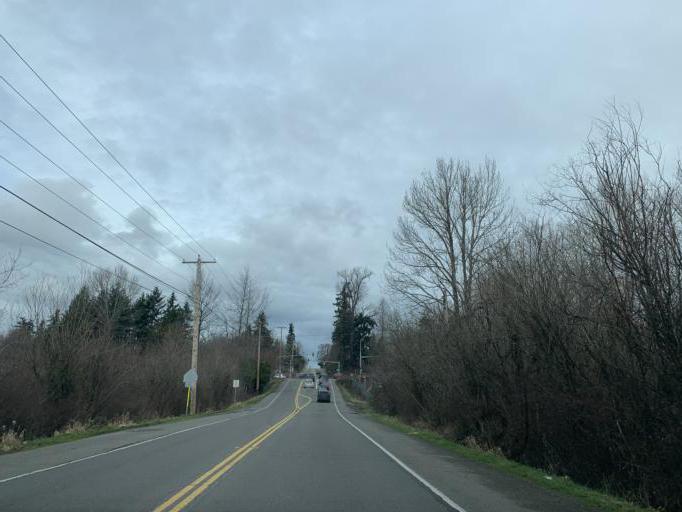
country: US
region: Washington
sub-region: King County
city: Lea Hill
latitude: 47.3616
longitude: -122.1762
